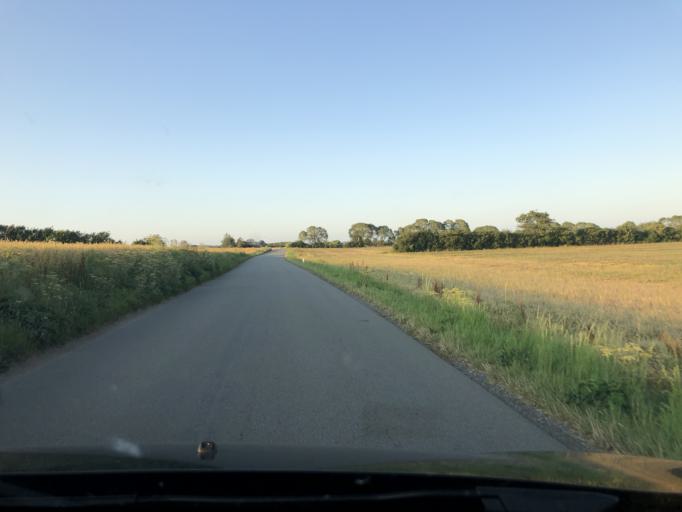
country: DK
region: South Denmark
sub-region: Vejle Kommune
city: Brejning
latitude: 55.6455
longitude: 9.7101
